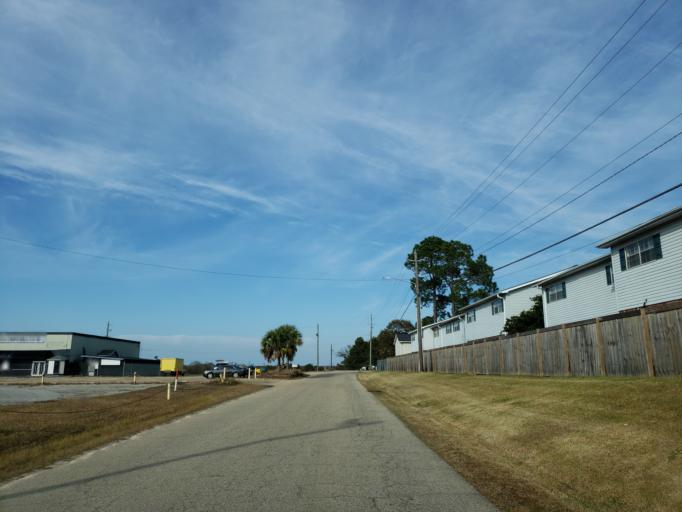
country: US
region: Mississippi
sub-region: Forrest County
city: Glendale
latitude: 31.3503
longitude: -89.3353
